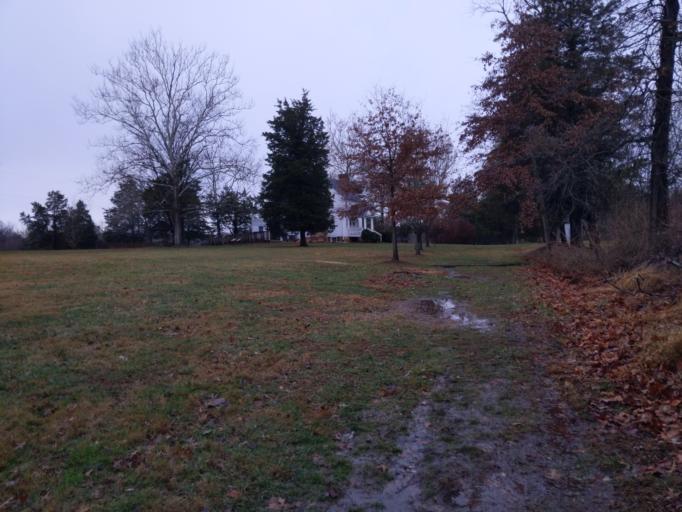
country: US
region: Virginia
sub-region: Loudoun County
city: Dulles Town Center
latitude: 39.0177
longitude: -77.4030
